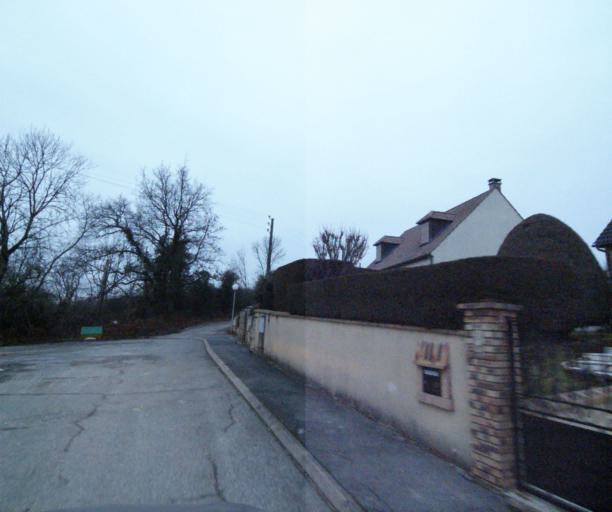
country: FR
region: Ile-de-France
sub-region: Departement de Seine-et-Marne
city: Longperrier
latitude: 49.0574
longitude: 2.6666
